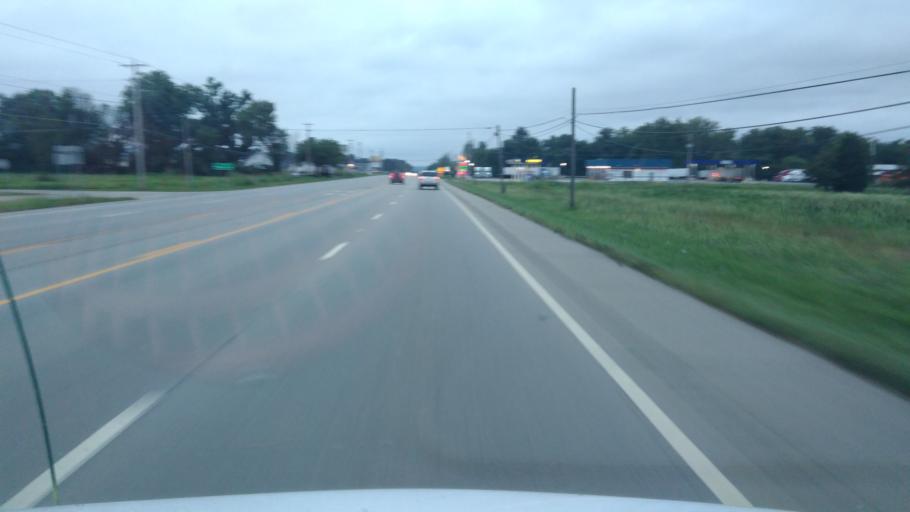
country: US
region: Ohio
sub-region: Pike County
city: Waverly
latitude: 39.1526
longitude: -82.9770
